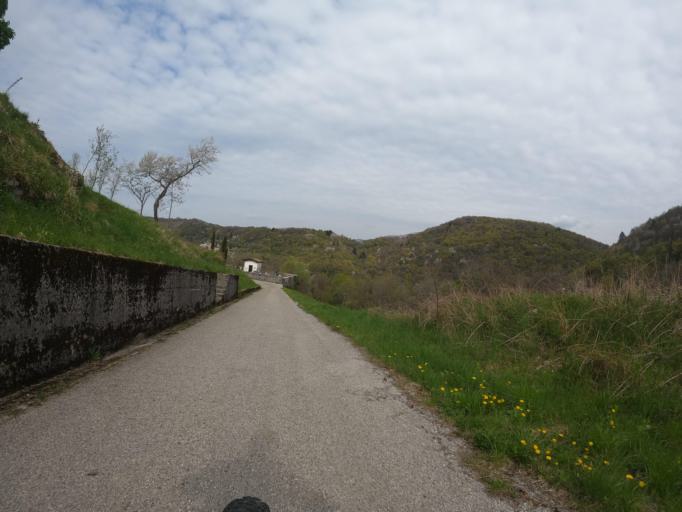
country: IT
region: Friuli Venezia Giulia
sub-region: Provincia di Udine
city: Stregna
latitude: 46.1376
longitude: 13.5911
